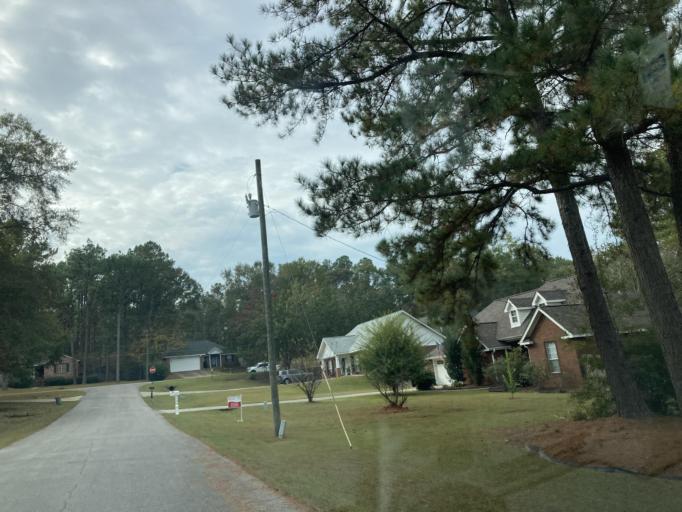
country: US
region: Mississippi
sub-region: Lamar County
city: West Hattiesburg
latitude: 31.2824
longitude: -89.3635
